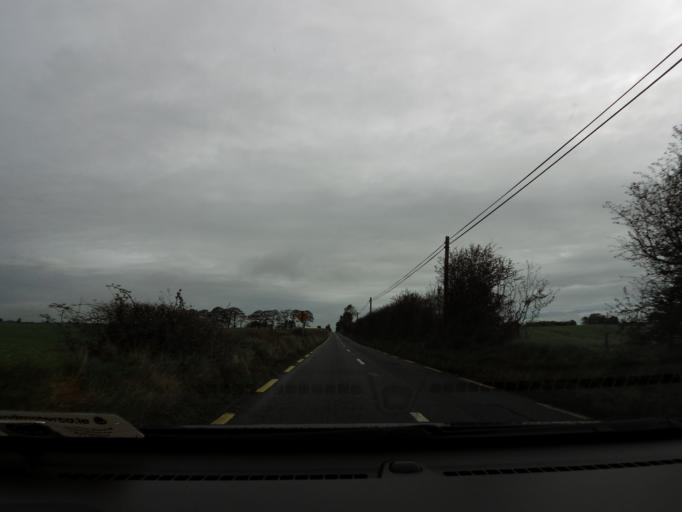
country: IE
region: Connaught
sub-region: County Galway
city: Tuam
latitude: 53.5846
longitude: -8.7792
